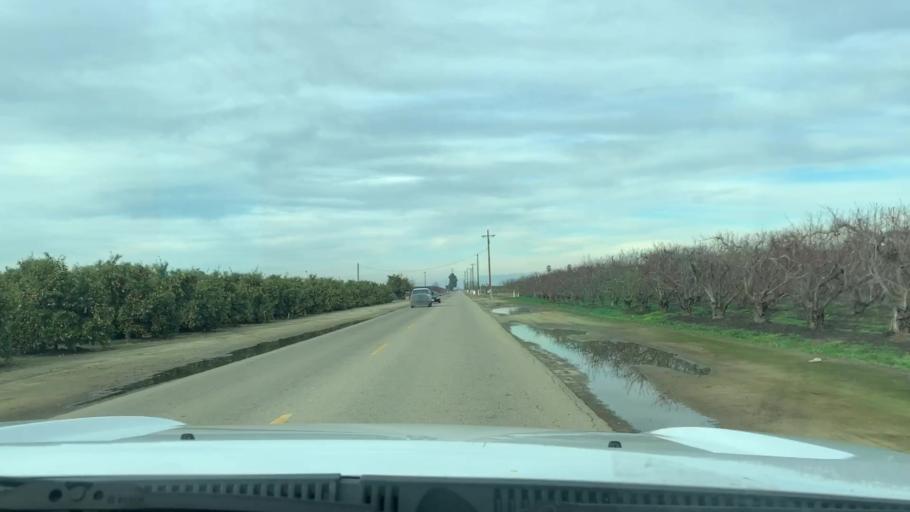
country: US
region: California
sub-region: Fresno County
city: Parlier
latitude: 36.6111
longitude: -119.5748
